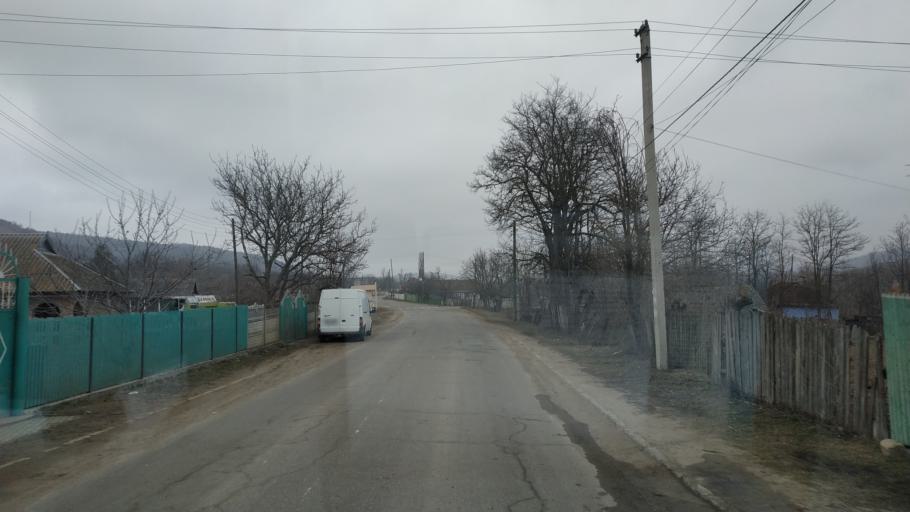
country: MD
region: Hincesti
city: Hincesti
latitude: 46.9822
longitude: 28.4511
